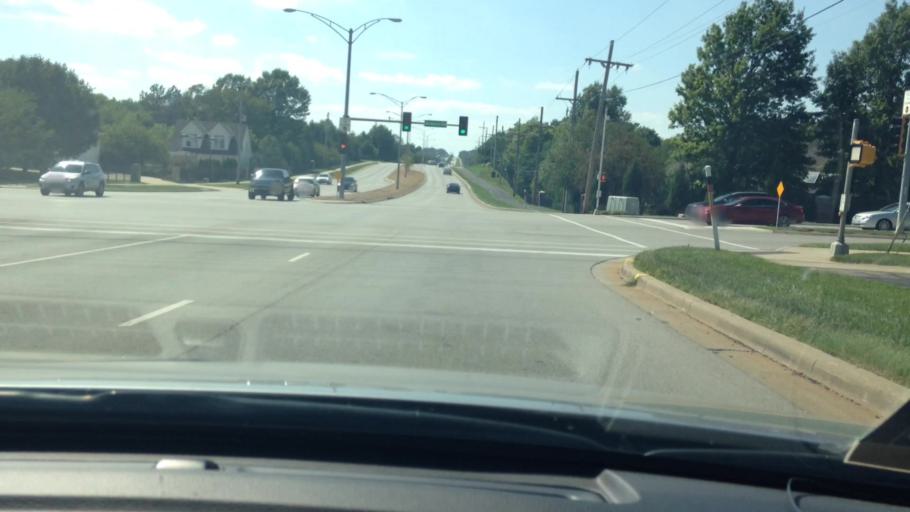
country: US
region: Kansas
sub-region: Johnson County
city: Lenexa
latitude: 38.8692
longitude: -94.6861
